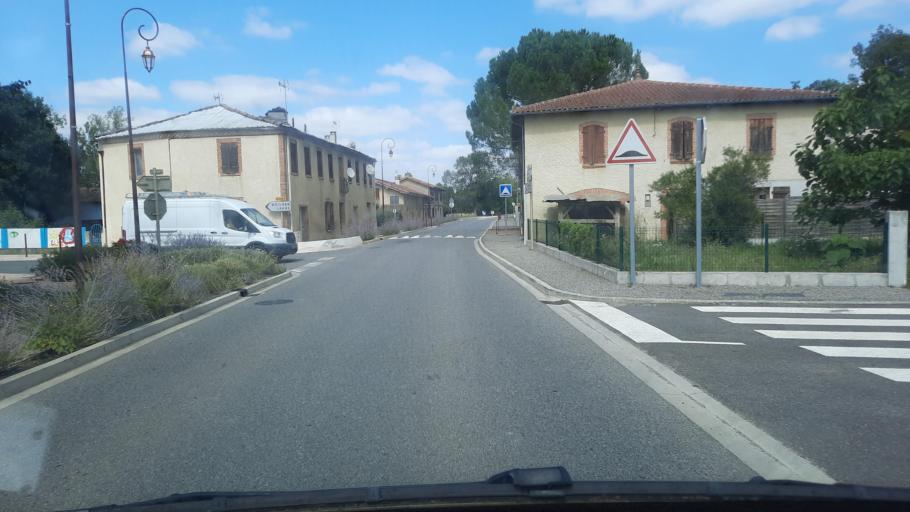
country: FR
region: Midi-Pyrenees
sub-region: Departement du Gers
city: Samatan
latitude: 43.5200
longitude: 0.9812
